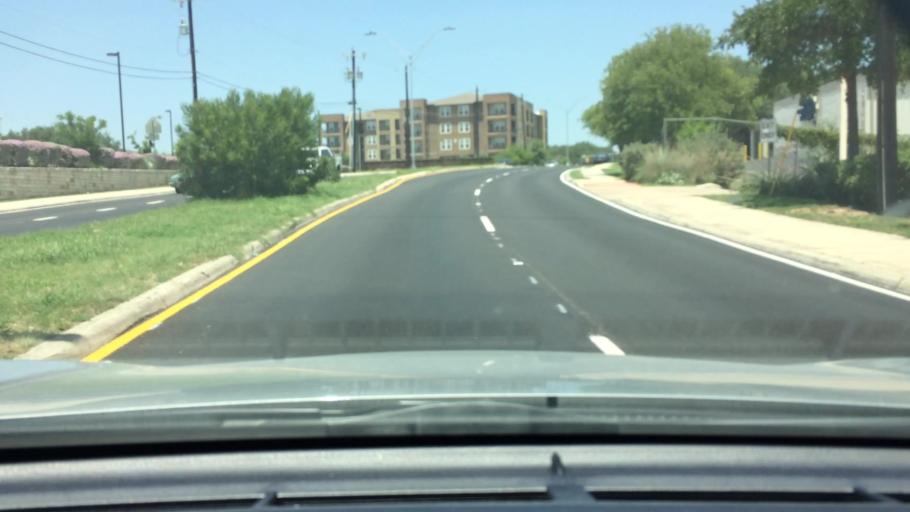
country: US
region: Texas
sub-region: Bexar County
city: Shavano Park
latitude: 29.5527
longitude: -98.5720
